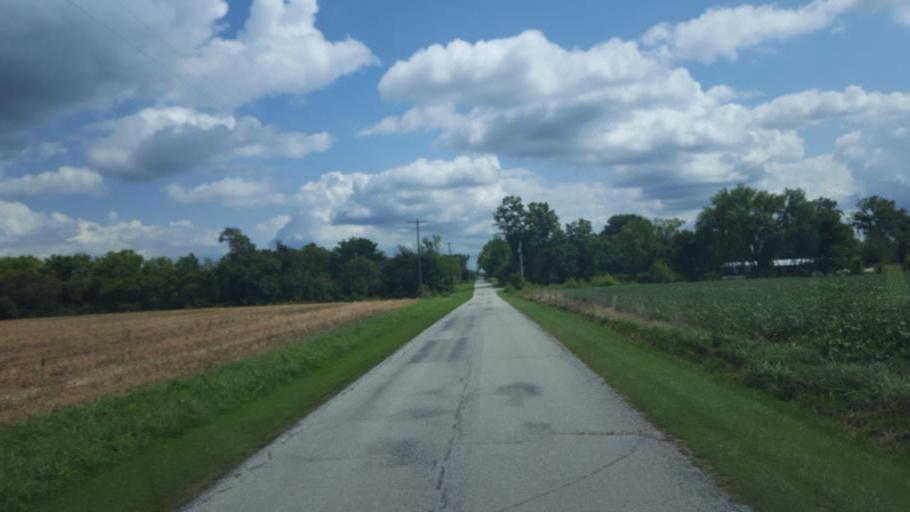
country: US
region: Ohio
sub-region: Huron County
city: Monroeville
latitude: 41.1760
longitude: -82.7327
